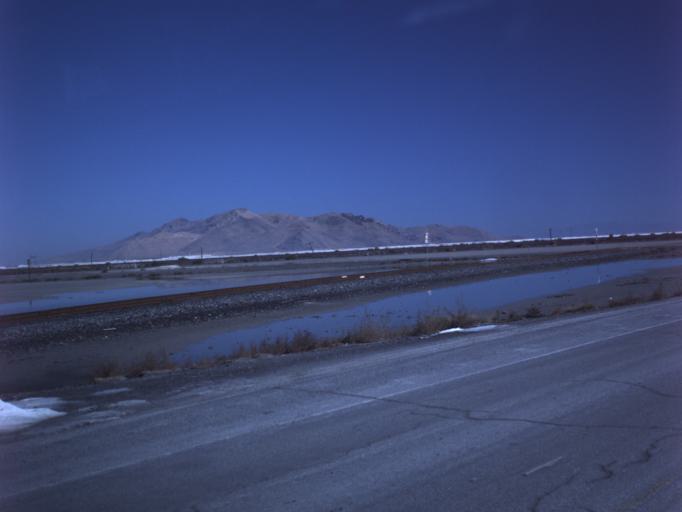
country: US
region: Utah
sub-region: Tooele County
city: Grantsville
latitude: 40.7103
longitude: -112.5286
